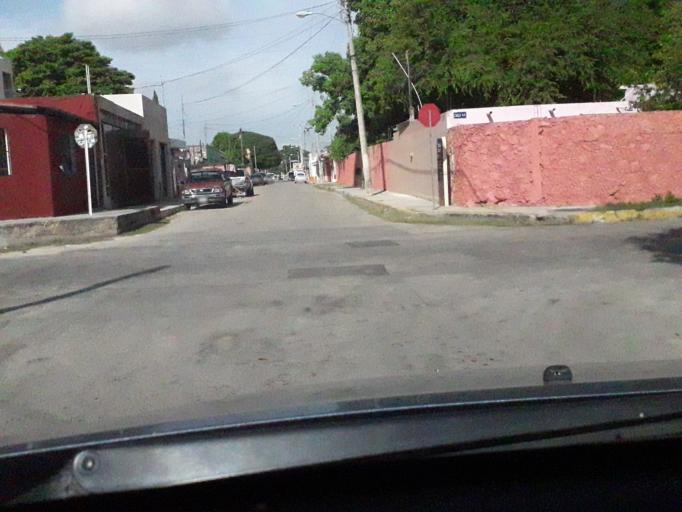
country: MX
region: Yucatan
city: Merida
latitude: 20.9556
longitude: -89.6152
